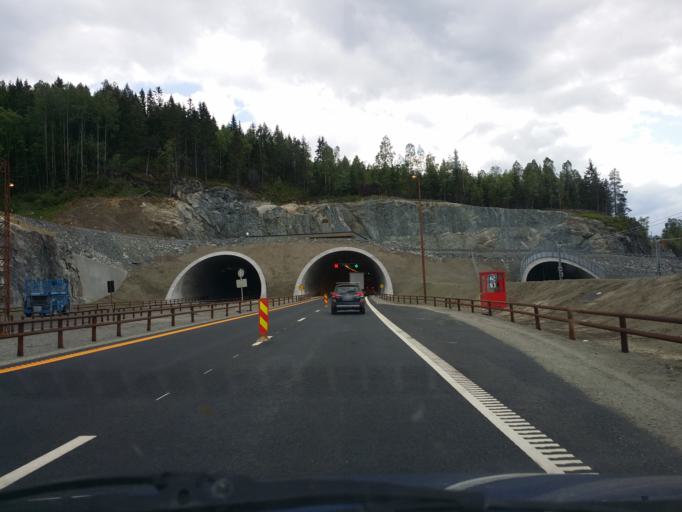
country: NO
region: Akershus
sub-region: Eidsvoll
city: Eidsvoll
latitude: 60.4399
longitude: 11.2418
